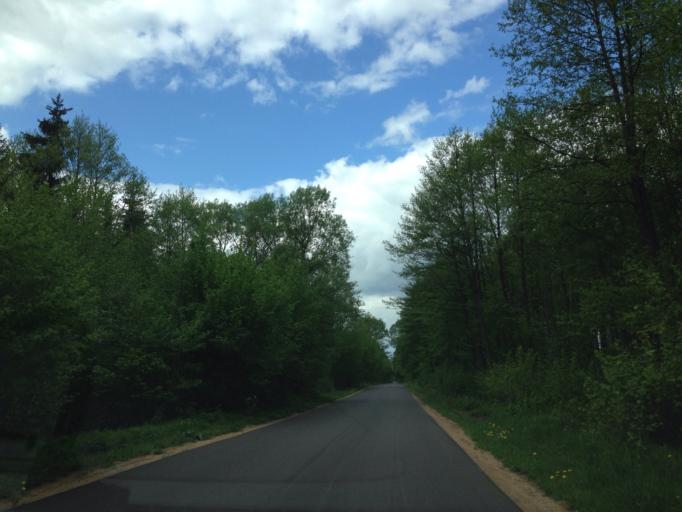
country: PL
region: Podlasie
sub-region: Powiat grajewski
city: Radzilow
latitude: 53.3247
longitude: 22.6009
